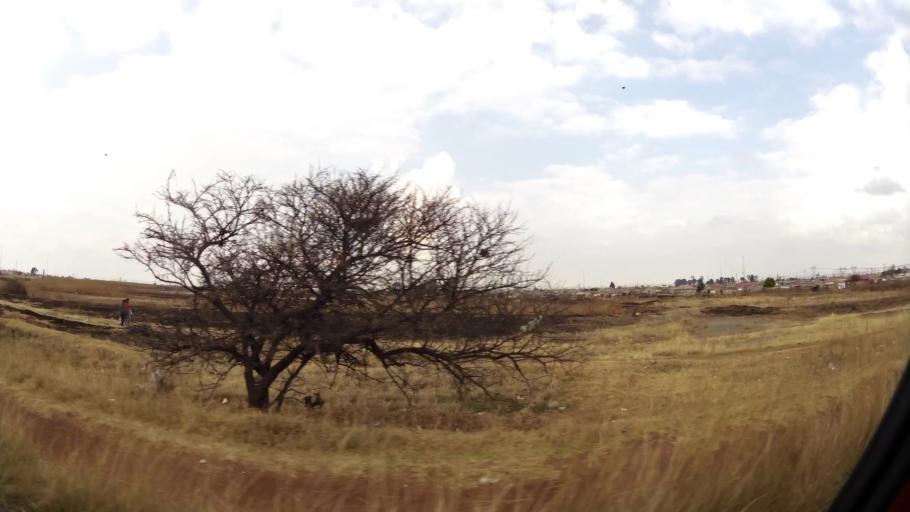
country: ZA
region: Gauteng
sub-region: Sedibeng District Municipality
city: Vanderbijlpark
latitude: -26.6715
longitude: 27.8607
